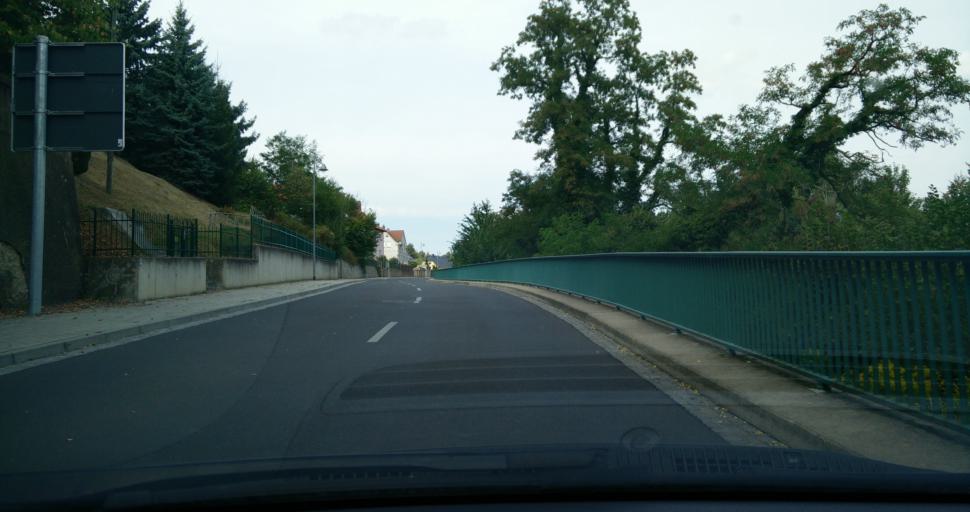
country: DE
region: Saxony
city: Colditz
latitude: 51.1246
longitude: 12.7986
